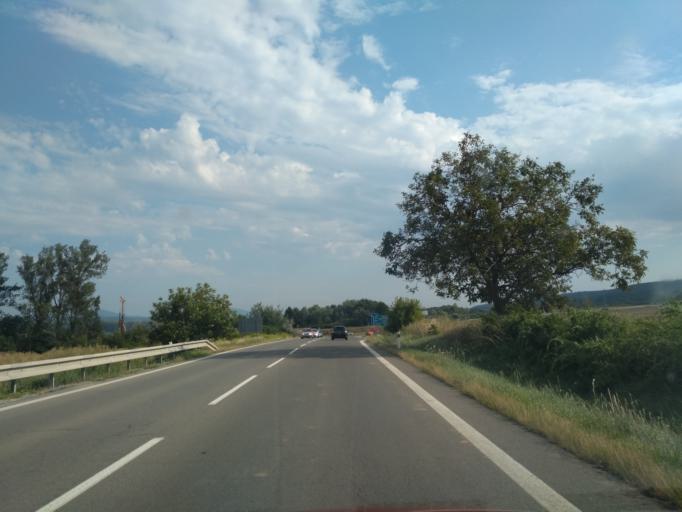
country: SK
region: Kosicky
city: Kosice
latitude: 48.7913
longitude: 21.3070
